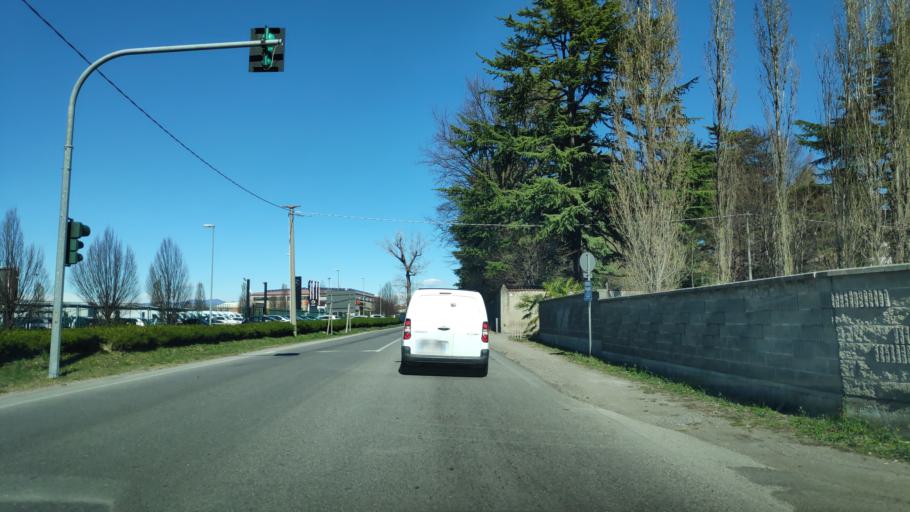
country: IT
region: Lombardy
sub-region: Provincia di Varese
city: Busto Arsizio
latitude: 45.6400
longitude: 8.8456
